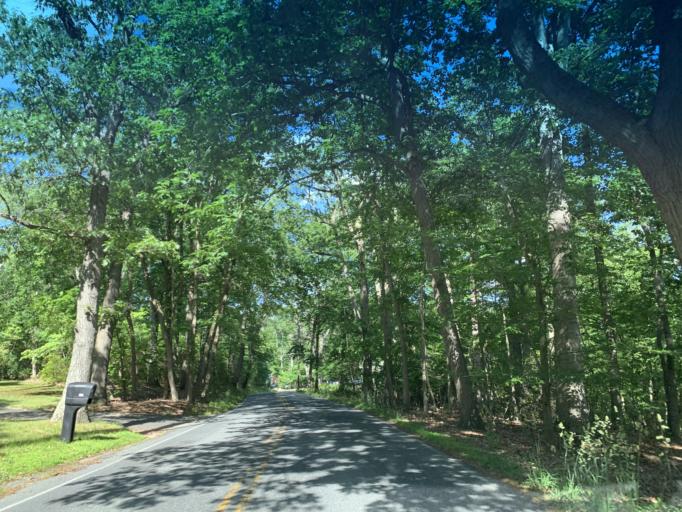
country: US
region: Maryland
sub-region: Cecil County
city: Charlestown
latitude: 39.5458
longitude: -75.9421
